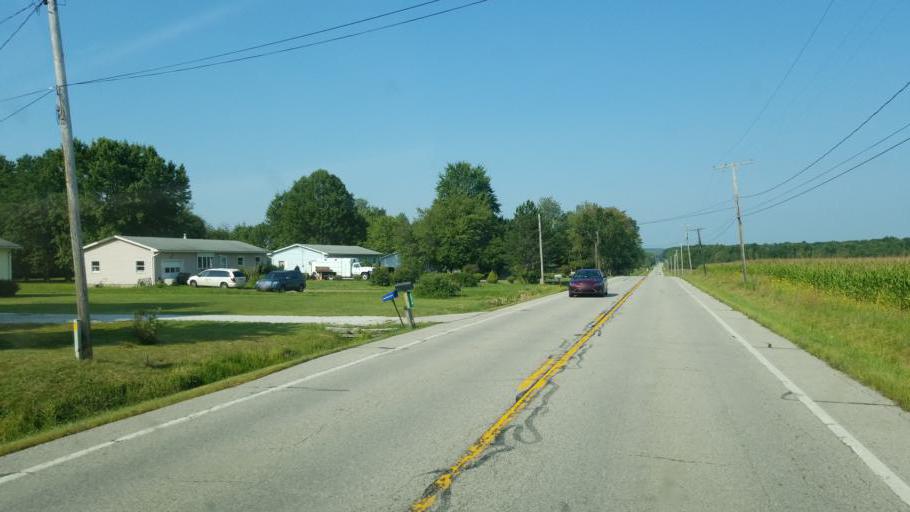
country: US
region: Ohio
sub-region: Ashtabula County
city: Roaming Shores
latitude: 41.6054
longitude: -80.8707
